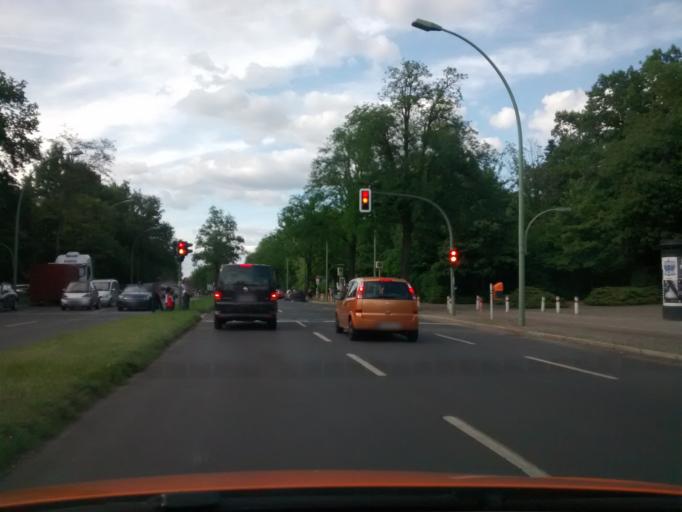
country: DE
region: Berlin
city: Schoneberg Bezirk
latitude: 52.4561
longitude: 13.3488
